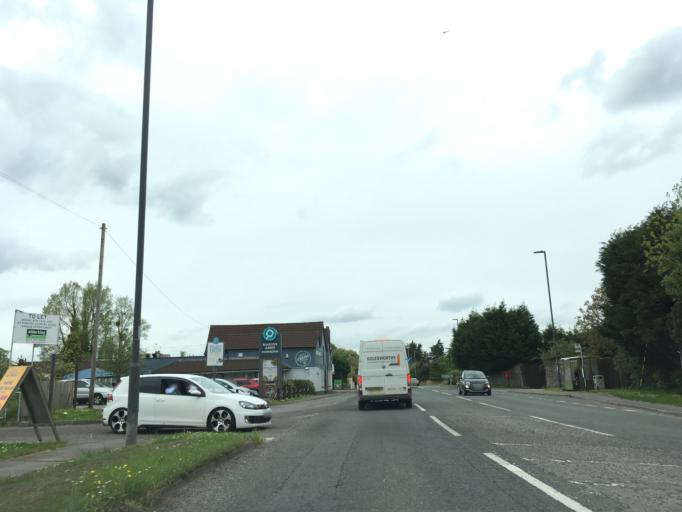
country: GB
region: England
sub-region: South Gloucestershire
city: Alveston
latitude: 51.5808
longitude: -2.5362
